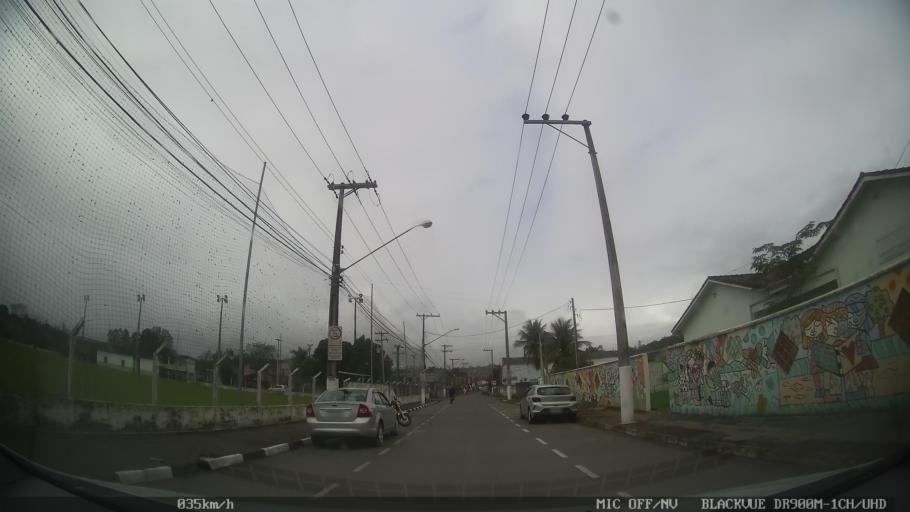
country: BR
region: Sao Paulo
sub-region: Cajati
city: Cajati
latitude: -24.7289
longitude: -48.1037
